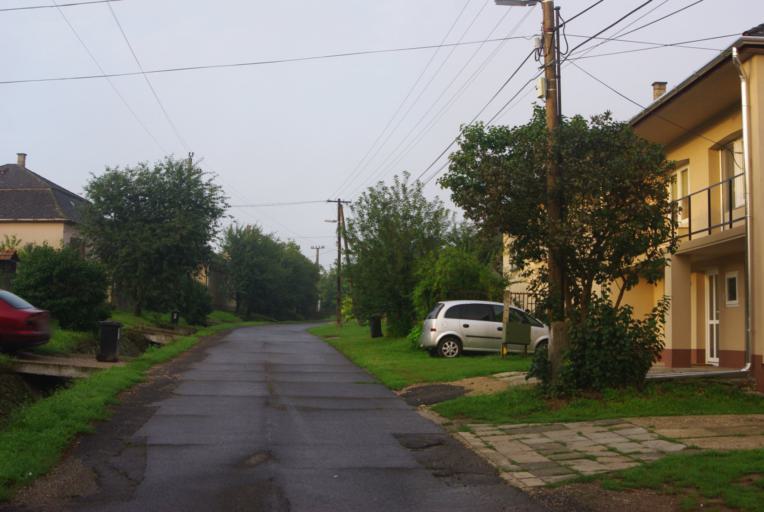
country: HU
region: Borsod-Abauj-Zemplen
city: Abaujszanto
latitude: 48.2763
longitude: 21.1887
